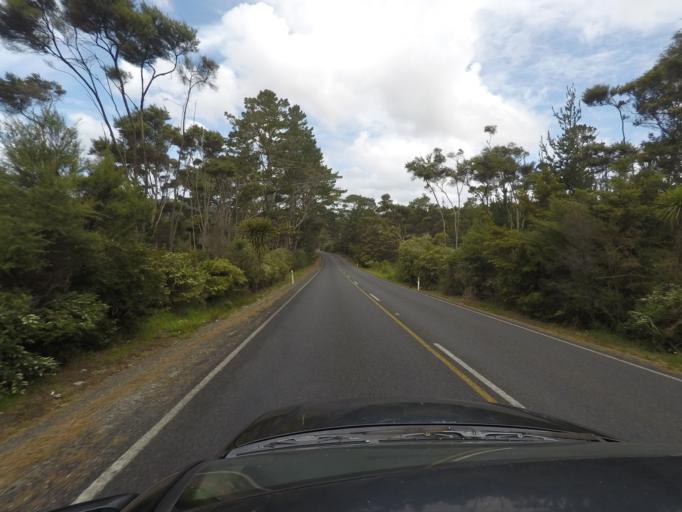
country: NZ
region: Auckland
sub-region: Auckland
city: Parakai
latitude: -36.6395
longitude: 174.5081
